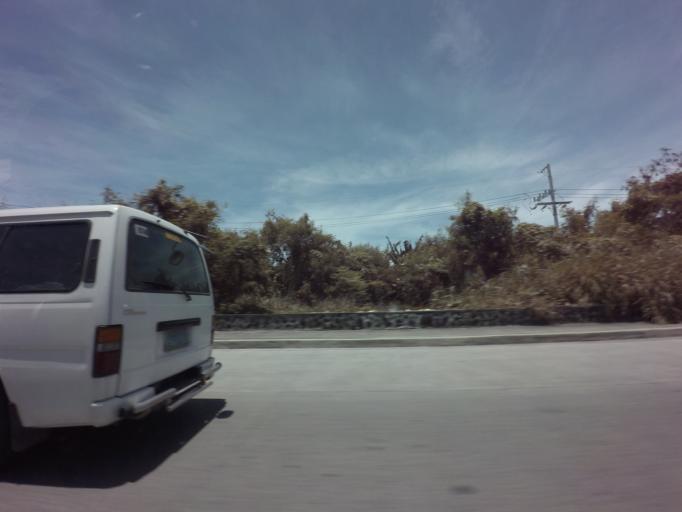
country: PH
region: Metro Manila
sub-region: Makati City
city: Makati City
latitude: 14.5026
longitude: 121.0198
